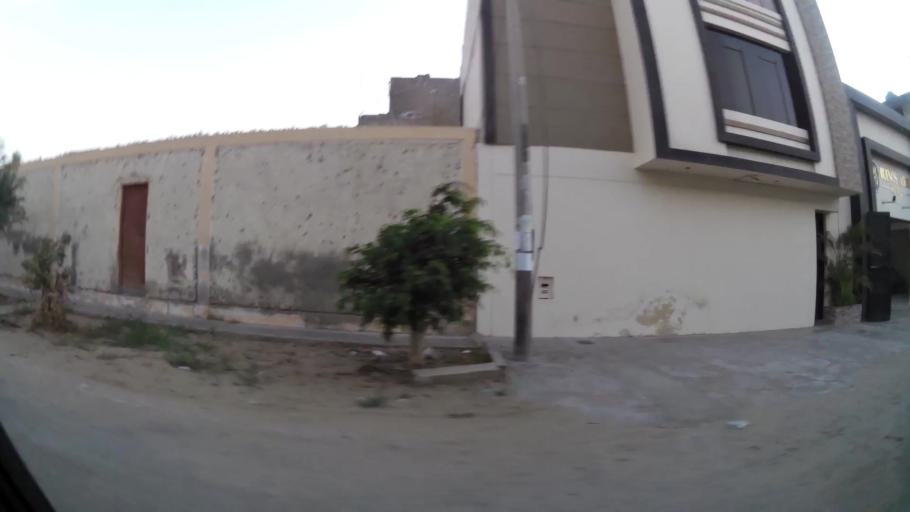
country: PE
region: Ancash
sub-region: Provincia de Santa
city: Buenos Aires
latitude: -9.1228
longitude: -78.5348
